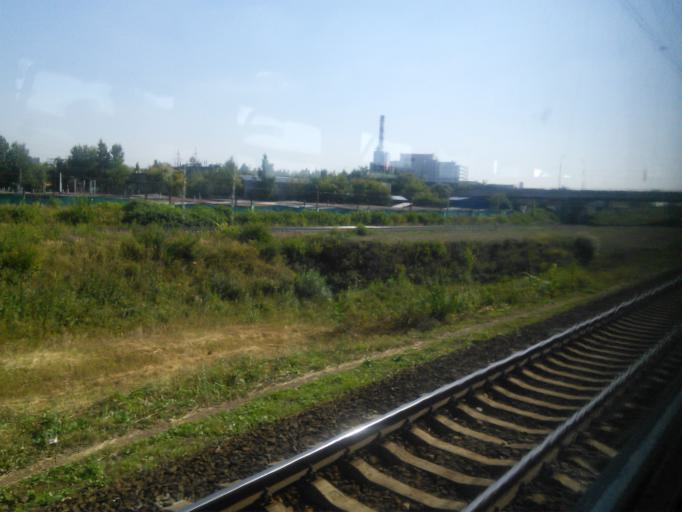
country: RU
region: Moskovskaya
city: Biryulevo Zapadnoye
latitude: 55.6060
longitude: 37.6351
